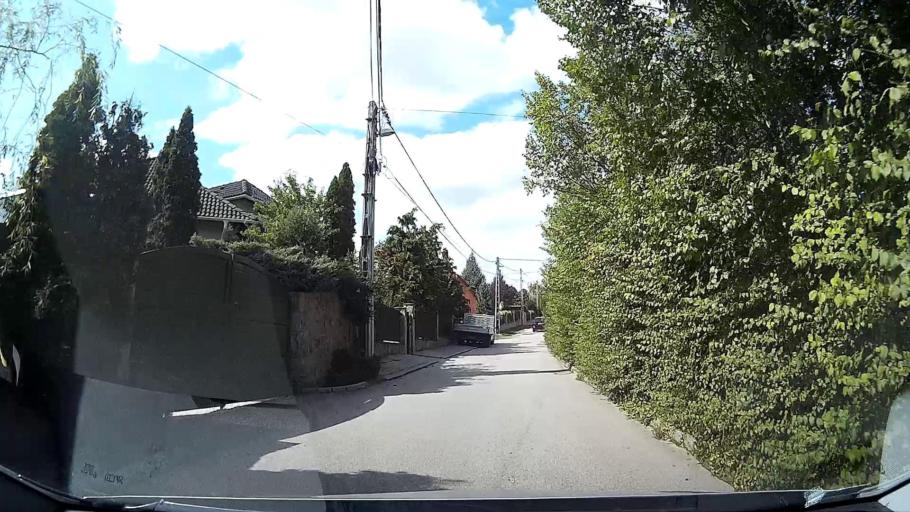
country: HU
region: Pest
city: Szentendre
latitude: 47.6856
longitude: 19.0745
